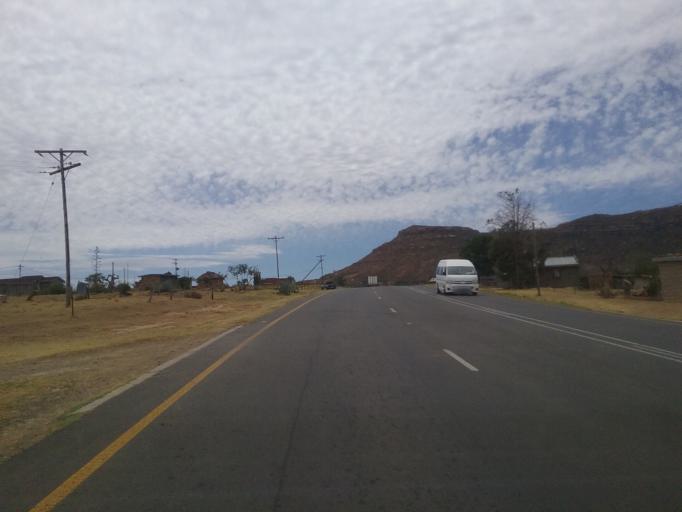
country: LS
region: Mafeteng
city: Mafeteng
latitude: -29.6457
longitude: 27.4665
